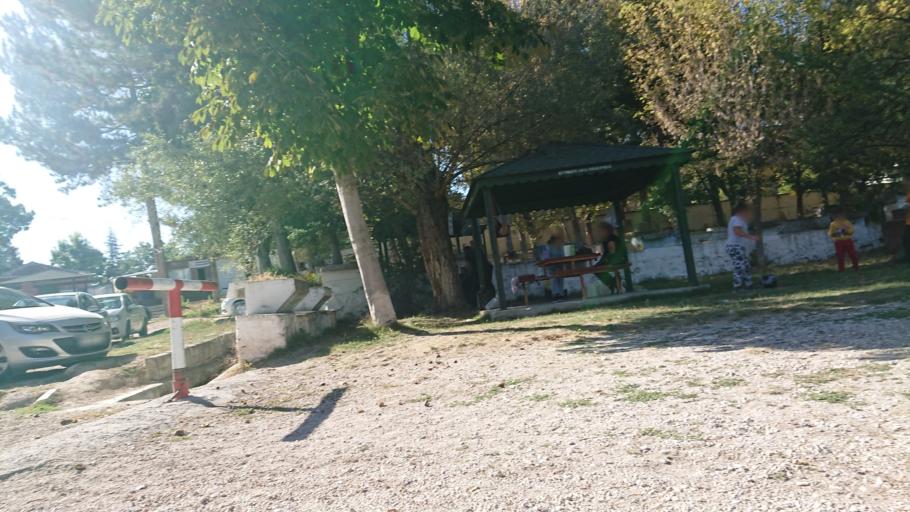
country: TR
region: Eskisehir
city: Cifteler
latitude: 39.3532
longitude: 31.0585
